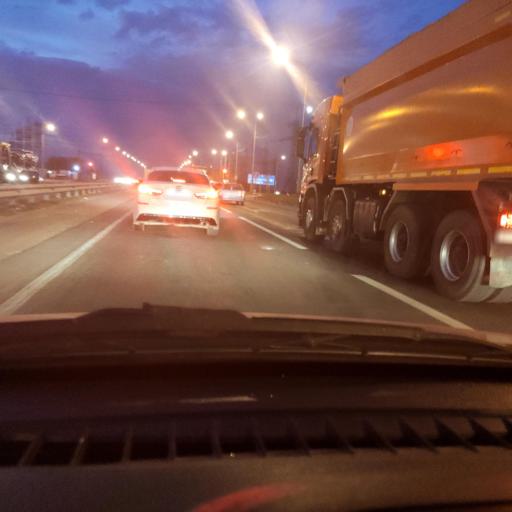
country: RU
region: Samara
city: Zhigulevsk
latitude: 53.5410
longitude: 49.5153
